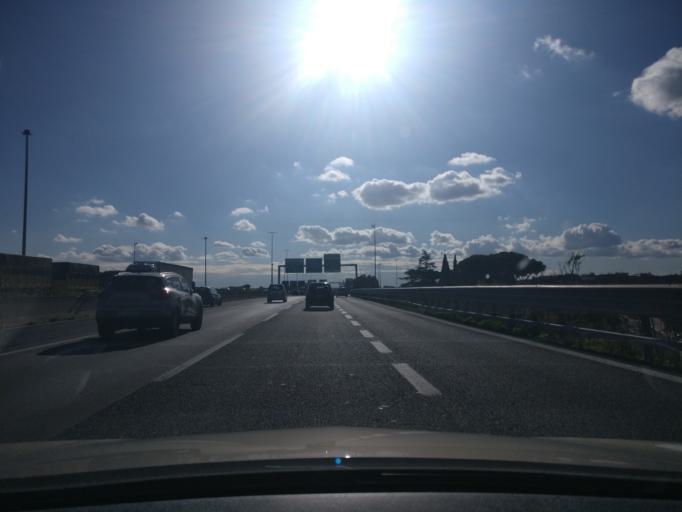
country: IT
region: Latium
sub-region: Citta metropolitana di Roma Capitale
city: Ciampino
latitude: 41.8386
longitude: 12.5907
